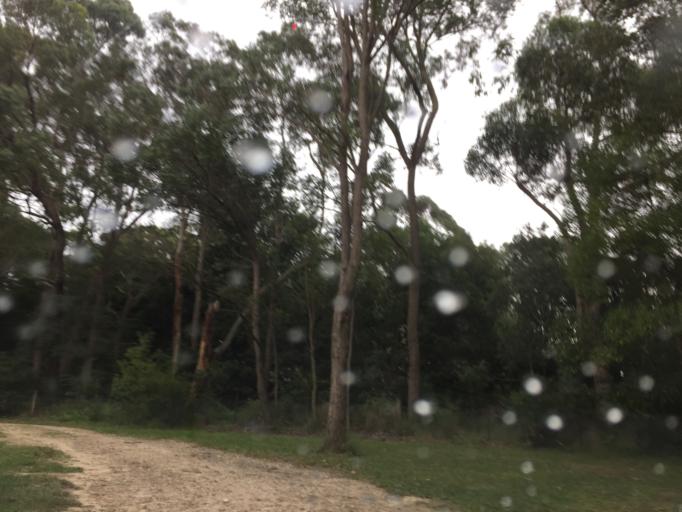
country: AU
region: New South Wales
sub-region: Hornsby Shire
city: Galston
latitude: -33.6548
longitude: 151.0580
